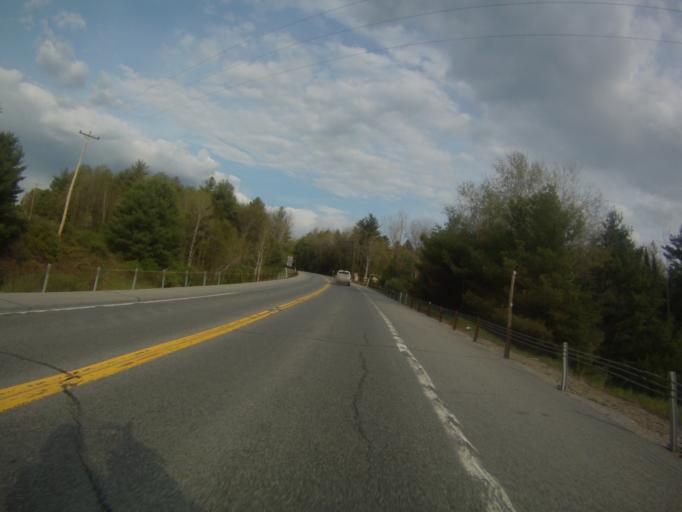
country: US
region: New York
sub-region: Warren County
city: Warrensburg
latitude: 43.6854
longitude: -73.9850
